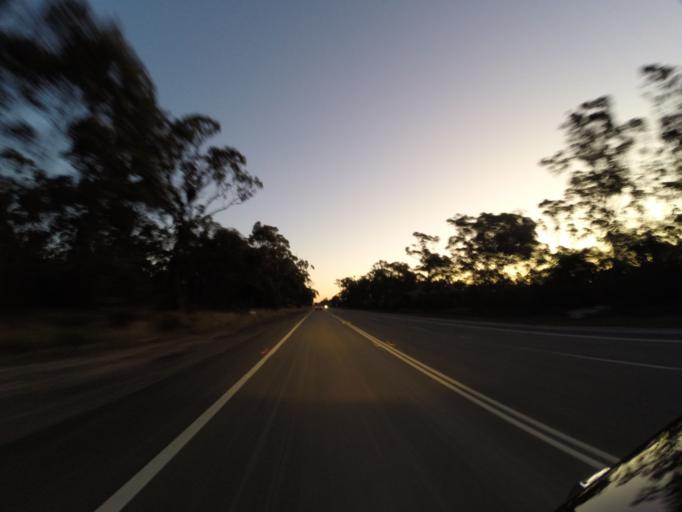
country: AU
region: New South Wales
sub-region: Liverpool
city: Holsworthy
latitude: -34.0243
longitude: 150.9707
